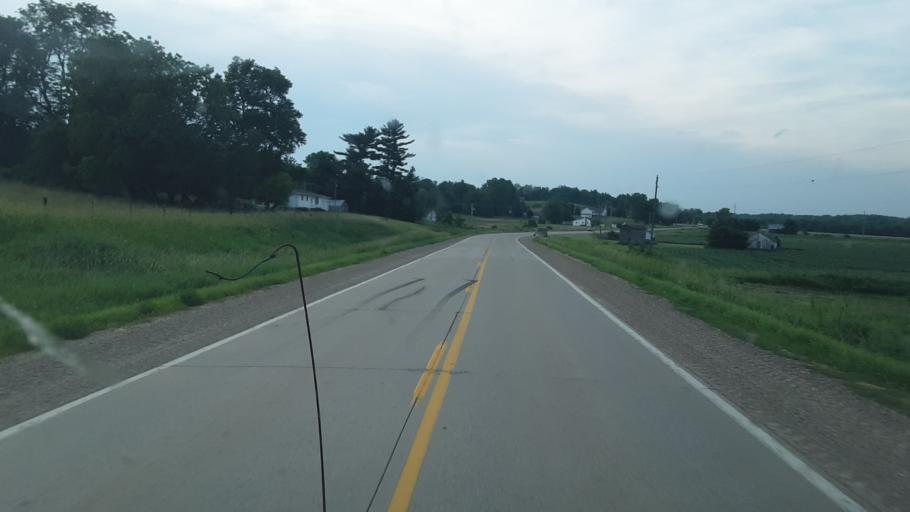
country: US
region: Iowa
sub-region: Tama County
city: Toledo
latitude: 41.9995
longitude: -92.7286
